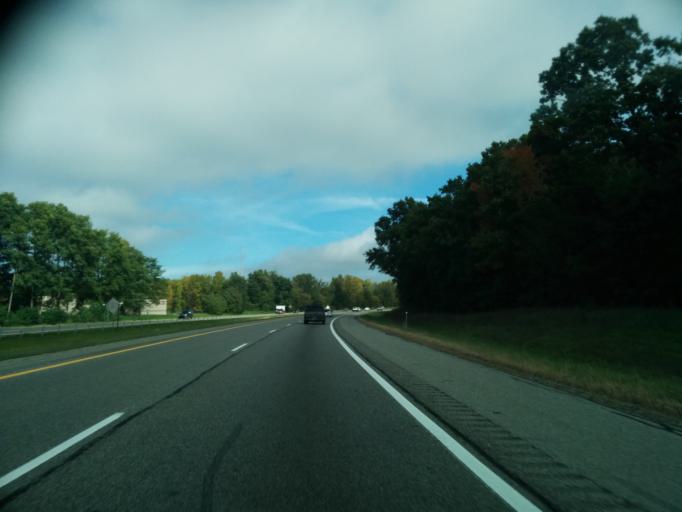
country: US
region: Michigan
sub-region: Livingston County
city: Brighton
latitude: 42.5486
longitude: -83.7493
